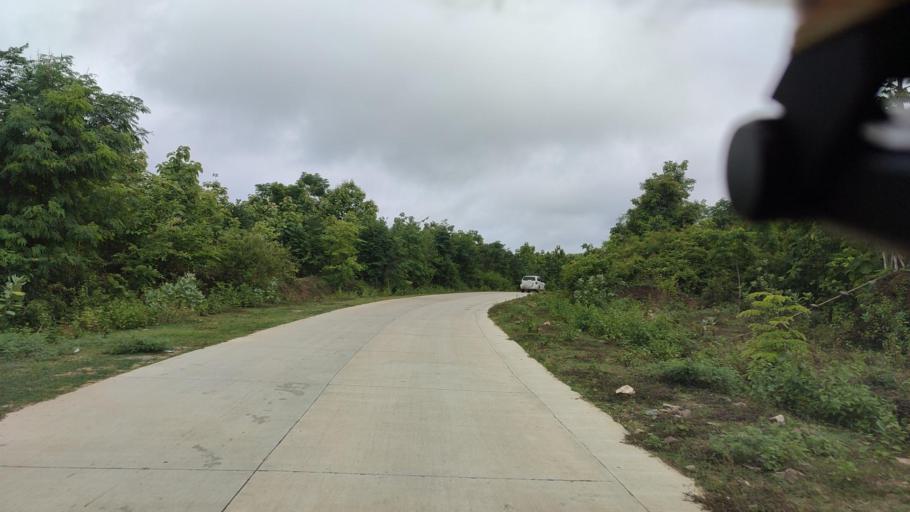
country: MM
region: Magway
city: Taungdwingyi
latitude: 20.0327
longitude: 95.7874
